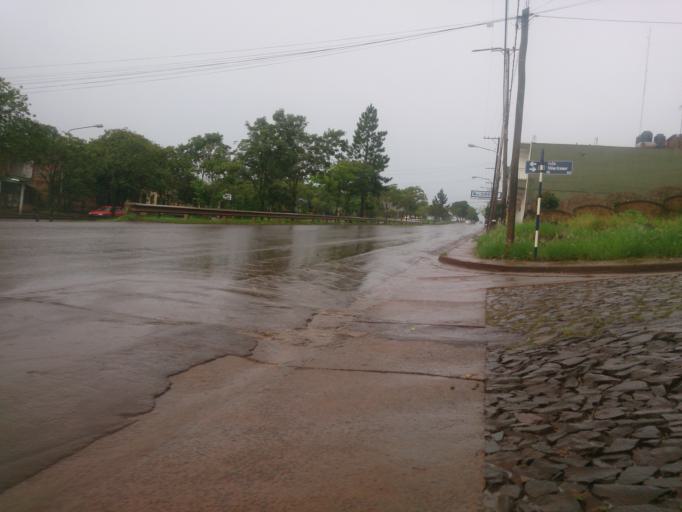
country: AR
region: Misiones
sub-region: Departamento de Obera
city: Obera
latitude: -27.4784
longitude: -55.1029
